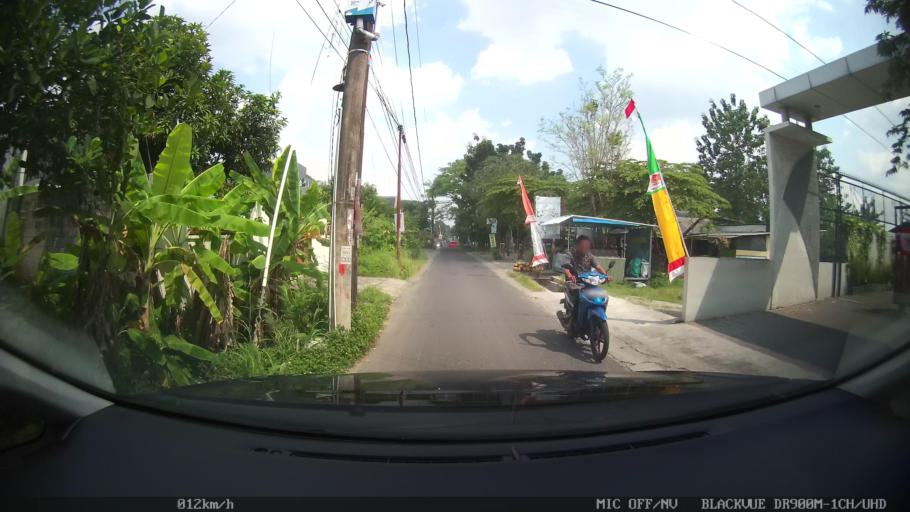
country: ID
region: Daerah Istimewa Yogyakarta
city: Depok
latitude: -7.7959
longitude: 110.4057
